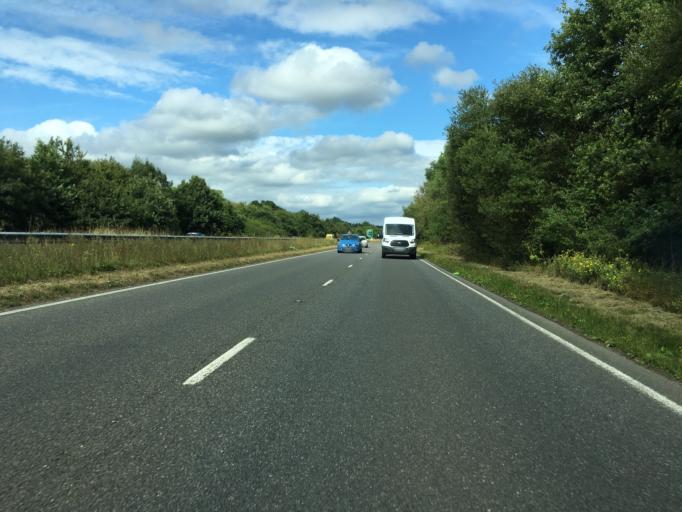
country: GB
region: England
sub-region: West Sussex
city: Horsham
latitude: 51.0745
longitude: -0.3451
